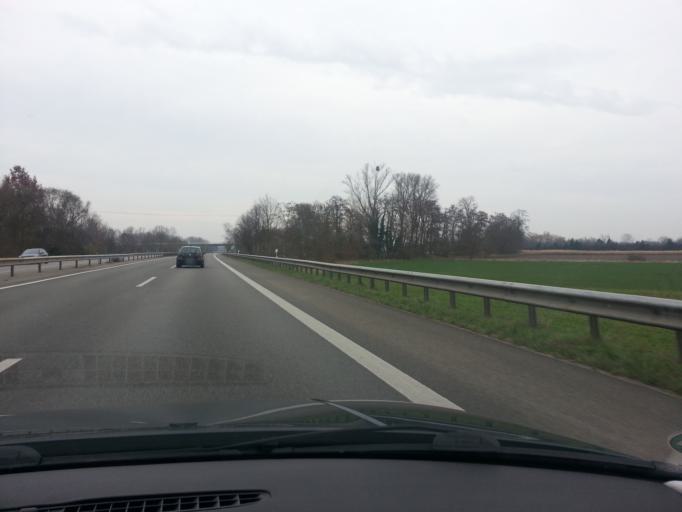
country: DE
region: Rheinland-Pfalz
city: Neuhofen
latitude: 49.4087
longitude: 8.4103
